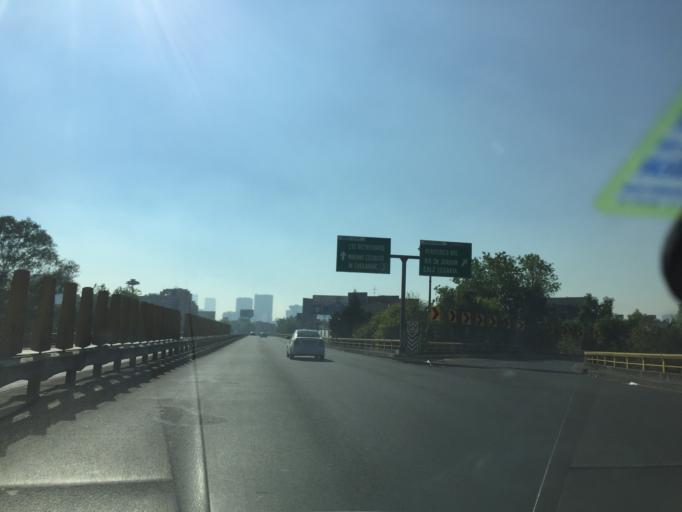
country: MX
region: Mexico City
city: Azcapotzalco
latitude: 19.4601
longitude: -99.1899
